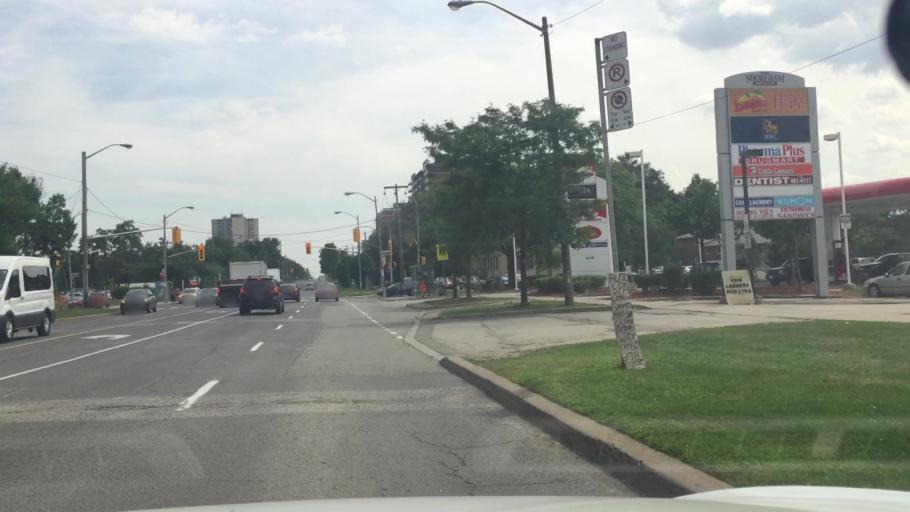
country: CA
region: Ontario
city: Concord
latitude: 43.7696
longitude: -79.5206
